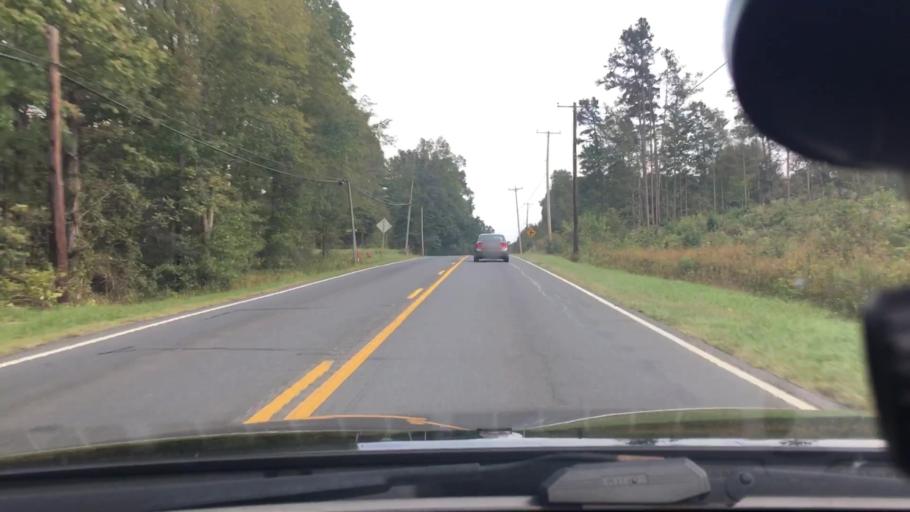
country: US
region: North Carolina
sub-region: Stanly County
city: Albemarle
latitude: 35.3237
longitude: -80.1273
